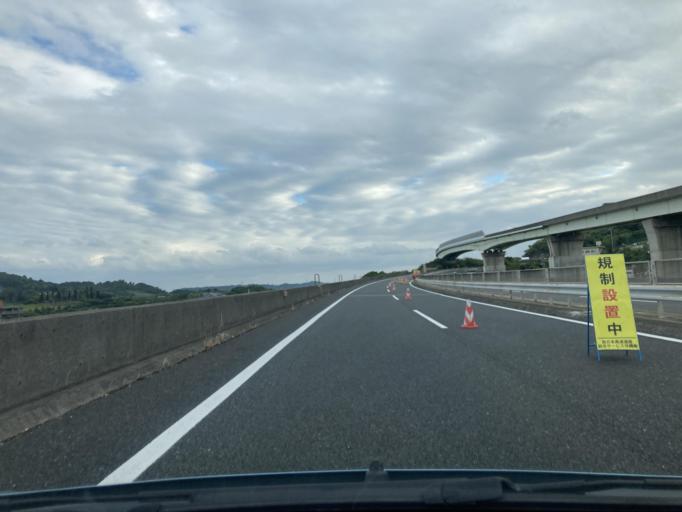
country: JP
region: Okinawa
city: Ginowan
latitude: 26.2205
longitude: 127.7390
